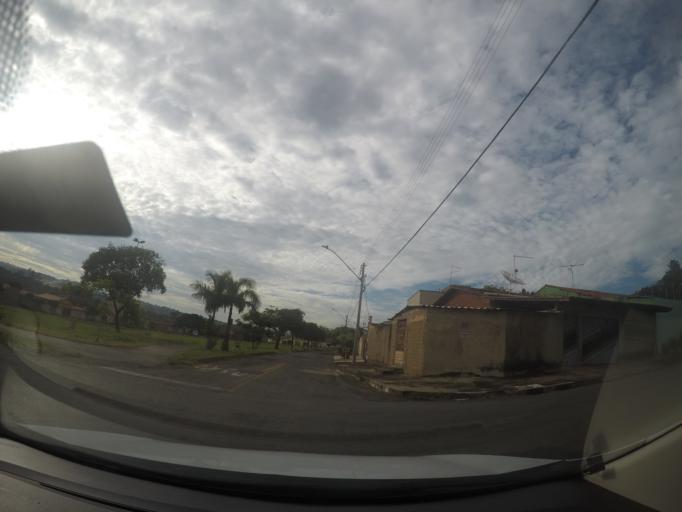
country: BR
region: Goias
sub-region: Goiania
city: Goiania
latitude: -16.6850
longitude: -49.2000
